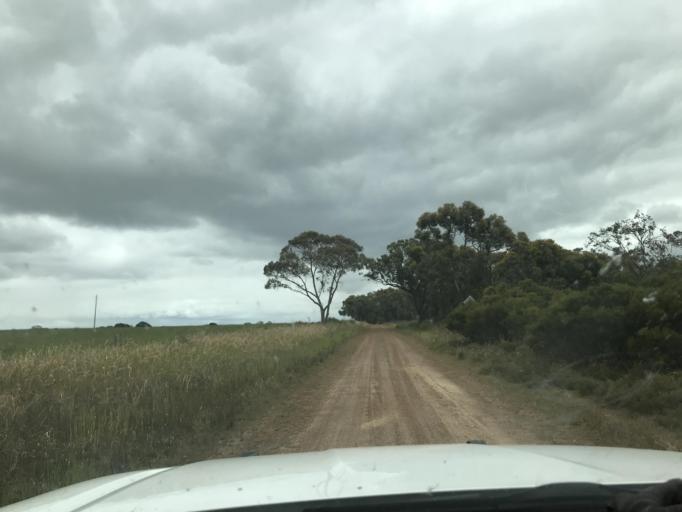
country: AU
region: South Australia
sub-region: Wattle Range
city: Penola
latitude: -37.0988
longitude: 141.2782
